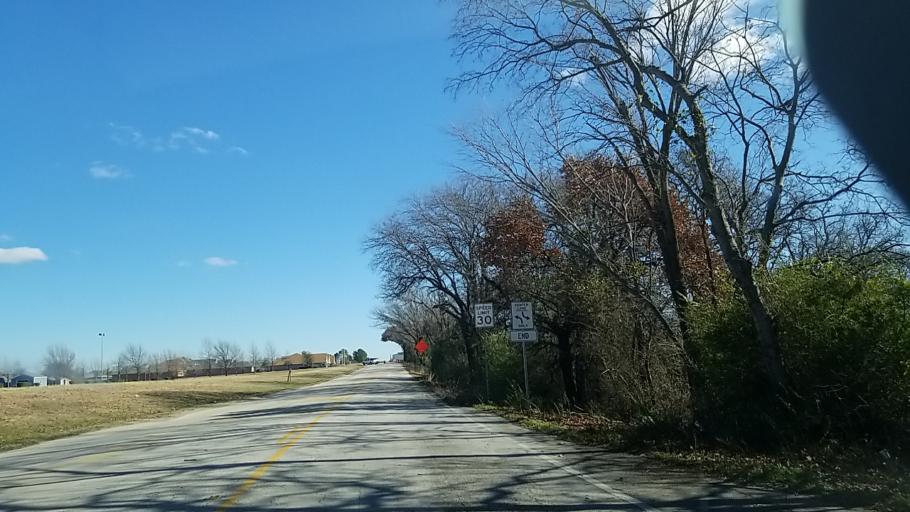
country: US
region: Texas
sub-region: Denton County
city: Denton
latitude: 33.1951
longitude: -97.0913
